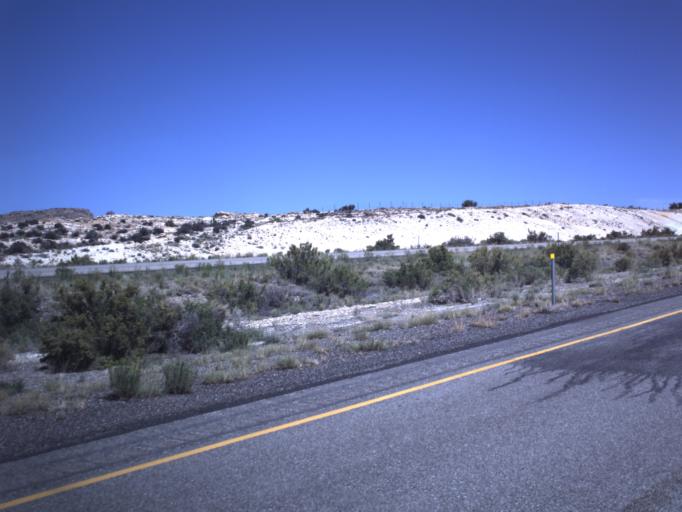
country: US
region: Utah
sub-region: Emery County
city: Ferron
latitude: 38.8152
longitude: -111.1920
